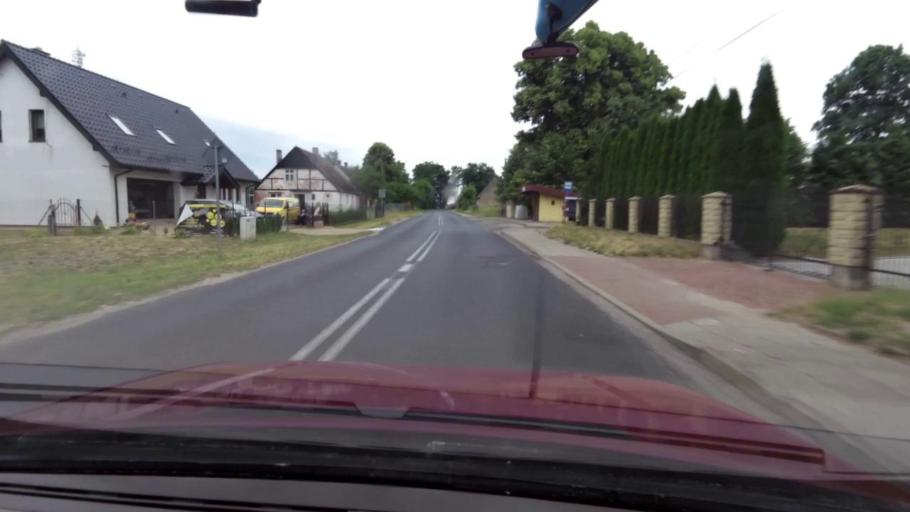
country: PL
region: West Pomeranian Voivodeship
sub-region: Powiat koszalinski
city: Sianow
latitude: 54.1623
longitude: 16.4432
